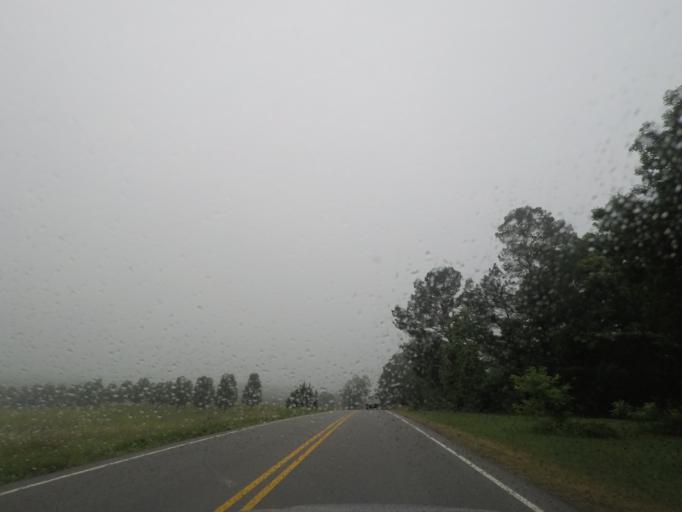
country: US
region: Virginia
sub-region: Prince Edward County
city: Farmville
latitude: 37.3827
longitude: -78.4847
